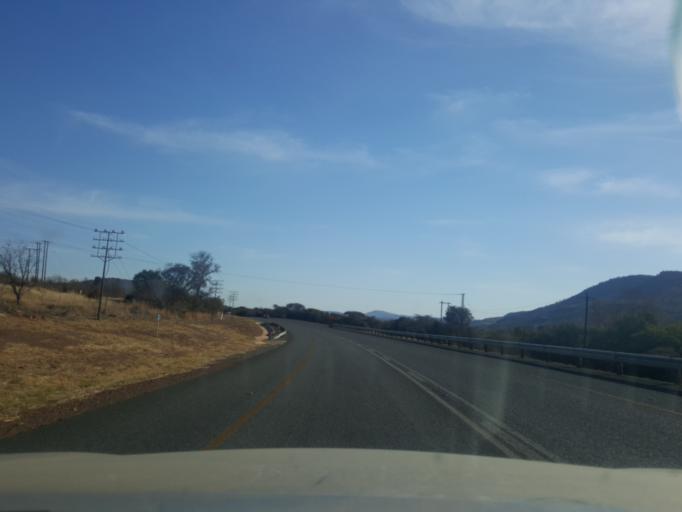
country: ZA
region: North-West
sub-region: Ngaka Modiri Molema District Municipality
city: Zeerust
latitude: -25.5340
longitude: 26.1338
